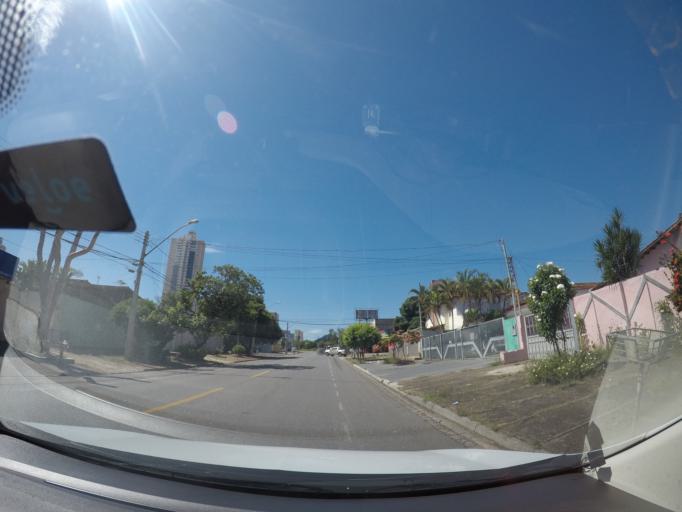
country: BR
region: Goias
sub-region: Goiania
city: Goiania
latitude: -16.7060
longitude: -49.2802
